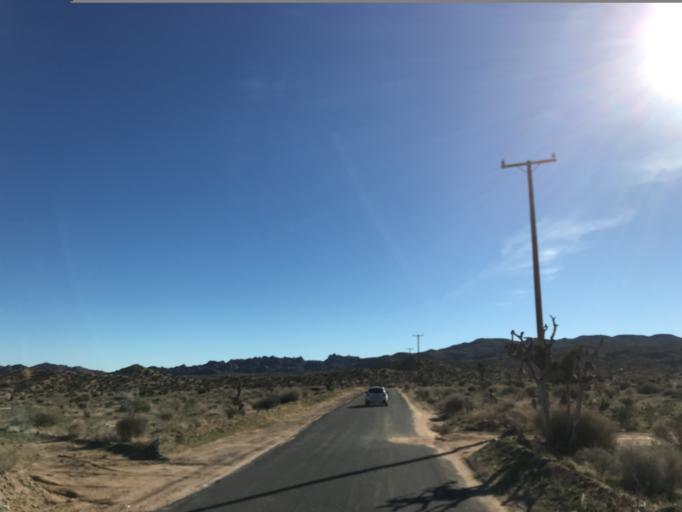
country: US
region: California
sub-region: San Bernardino County
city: Yucca Valley
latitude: 34.1948
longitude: -116.5461
